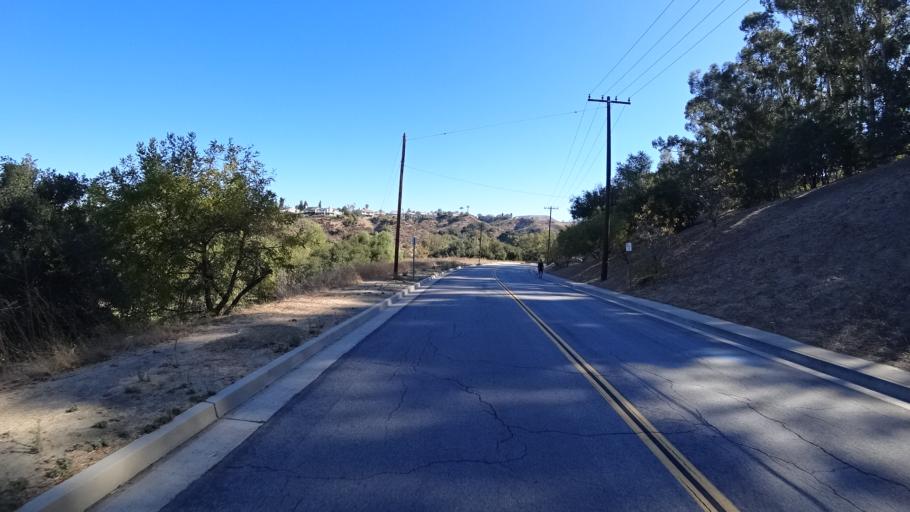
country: US
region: California
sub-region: Orange County
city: Villa Park
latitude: 33.8409
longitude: -117.7614
